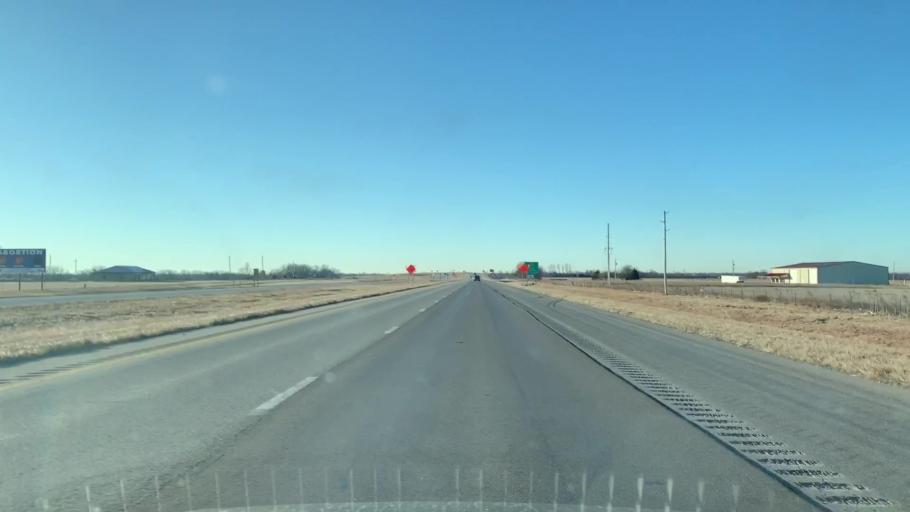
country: US
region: Kansas
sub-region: Bourbon County
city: Fort Scott
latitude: 37.7789
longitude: -94.7054
